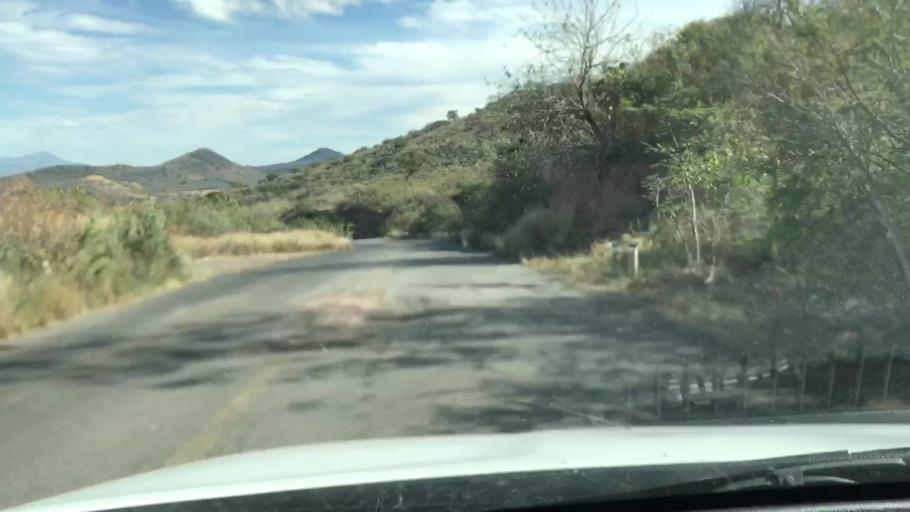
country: MX
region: Jalisco
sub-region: Zacoalco de Torres
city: Barranca de Otates (Barranca de Otatan)
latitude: 20.2568
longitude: -103.6729
